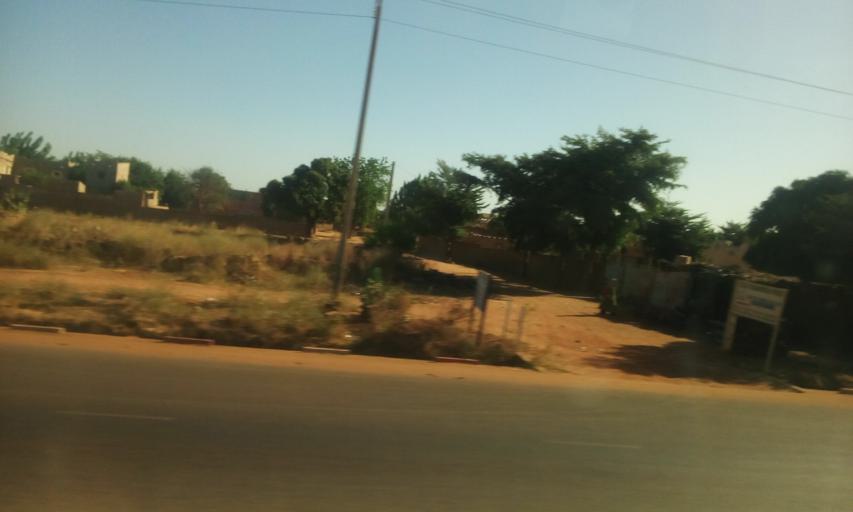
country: ML
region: Segou
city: Segou
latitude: 13.4170
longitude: -6.3101
